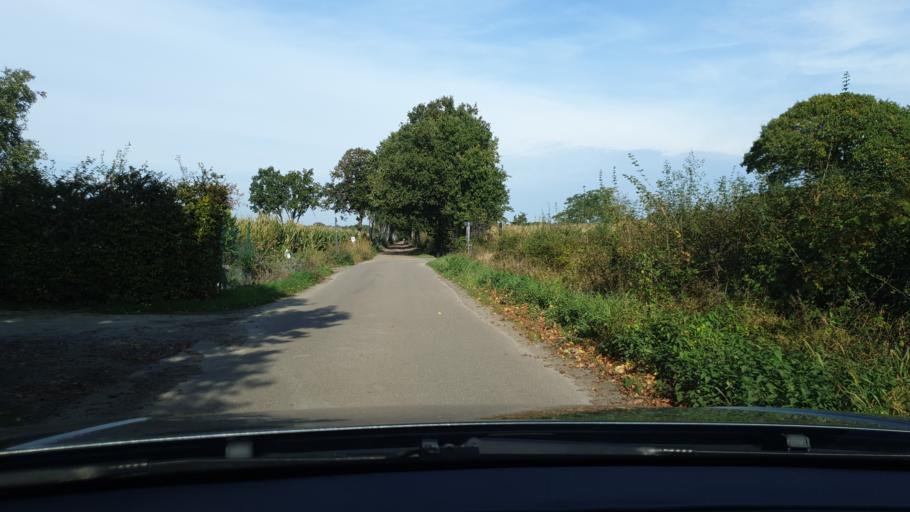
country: BE
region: Flanders
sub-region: Provincie Antwerpen
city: Laakdal
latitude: 51.1254
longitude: 5.0257
